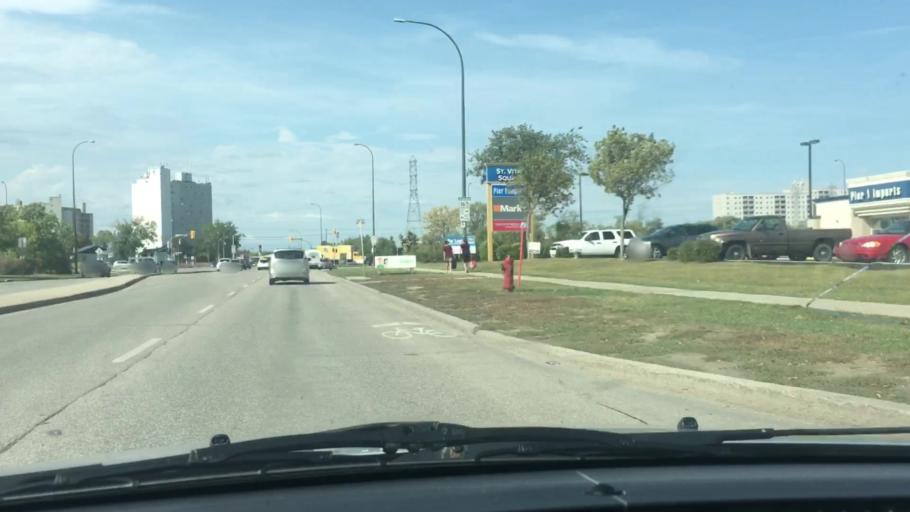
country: CA
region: Manitoba
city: Winnipeg
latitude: 49.8312
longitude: -97.1074
